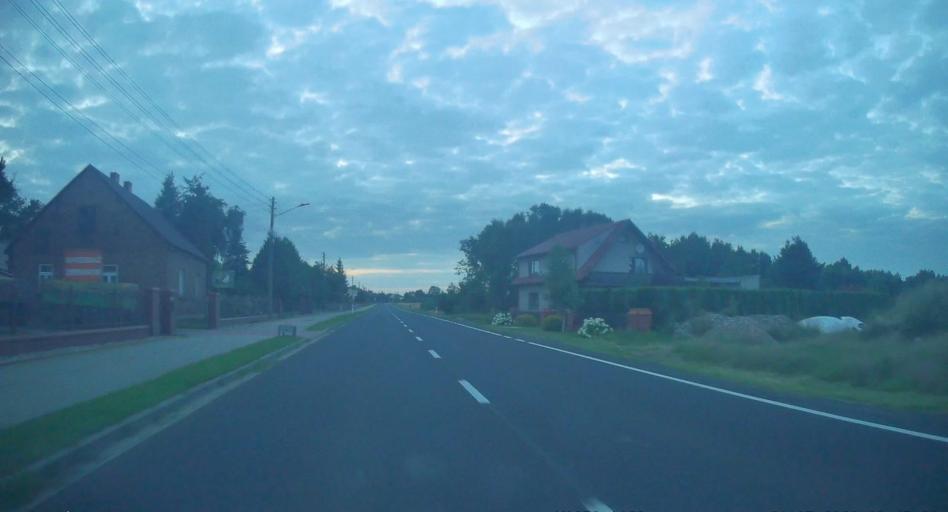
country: PL
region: Silesian Voivodeship
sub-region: Powiat klobucki
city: Starokrzepice
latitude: 51.0022
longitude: 18.6638
